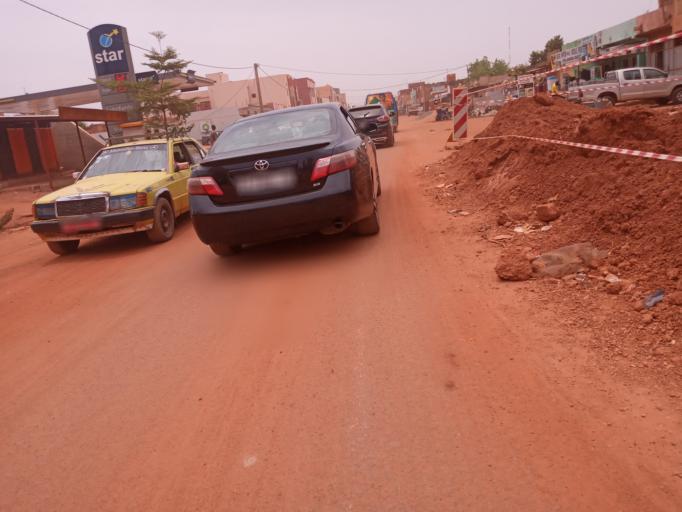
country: ML
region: Bamako
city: Bamako
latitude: 12.5791
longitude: -8.0158
